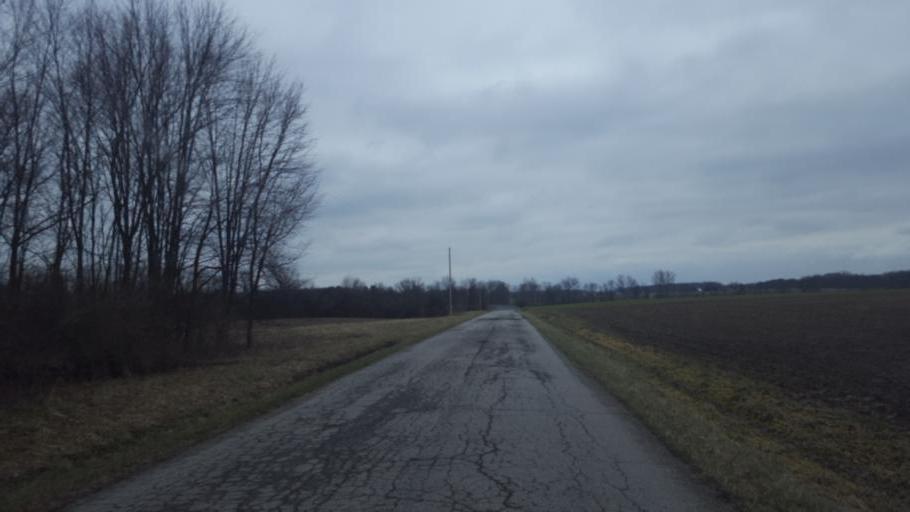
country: US
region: Ohio
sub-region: Delaware County
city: Ashley
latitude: 40.4197
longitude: -83.0097
